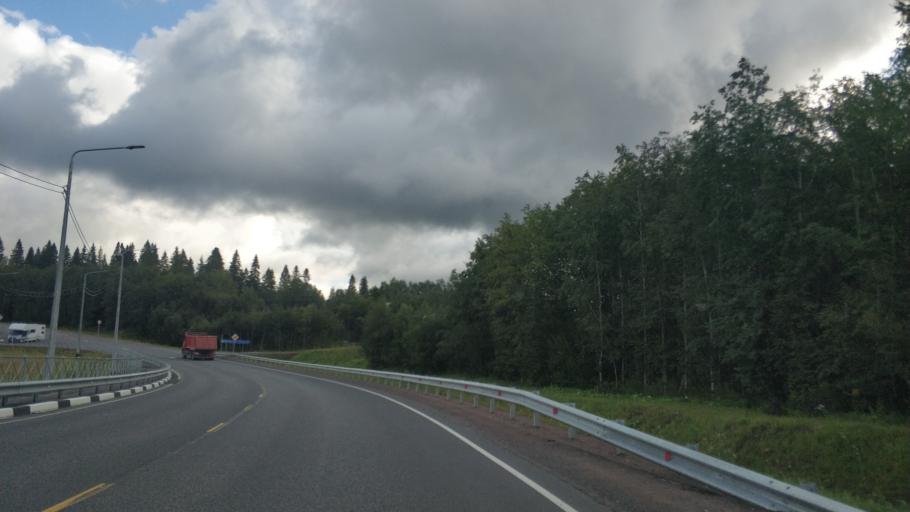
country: RU
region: Republic of Karelia
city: Ruskeala
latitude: 61.9451
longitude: 30.5976
